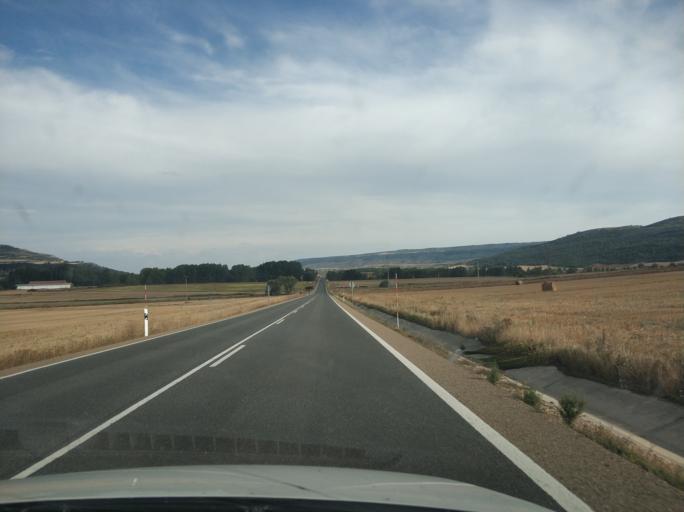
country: ES
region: Castille and Leon
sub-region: Provincia de Palencia
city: Pomar de Valdivia
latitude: 42.7673
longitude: -4.1926
